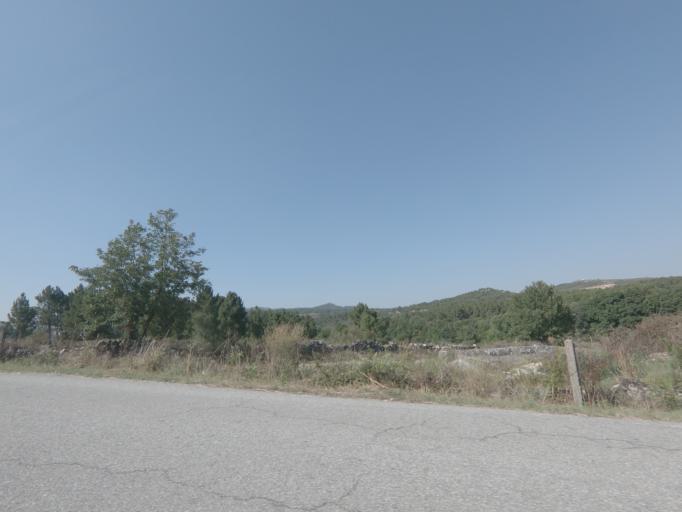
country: PT
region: Viseu
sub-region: Moimenta da Beira
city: Moimenta da Beira
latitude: 40.9717
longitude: -7.5845
